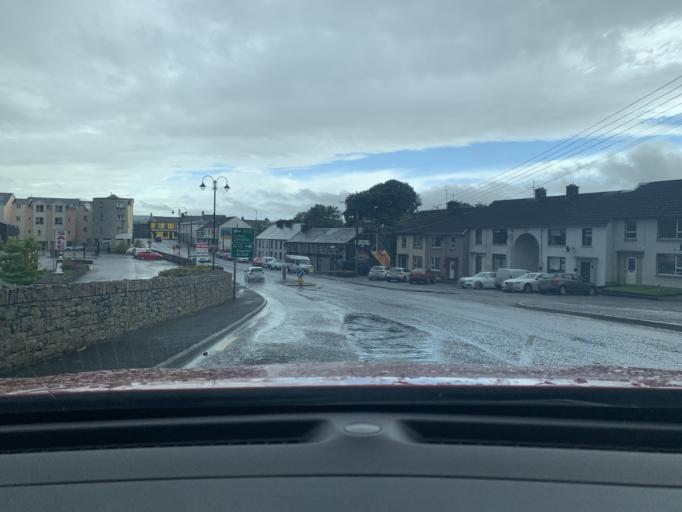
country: IE
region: Ulster
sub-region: County Donegal
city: Ballybofey
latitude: 54.8067
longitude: -7.7685
